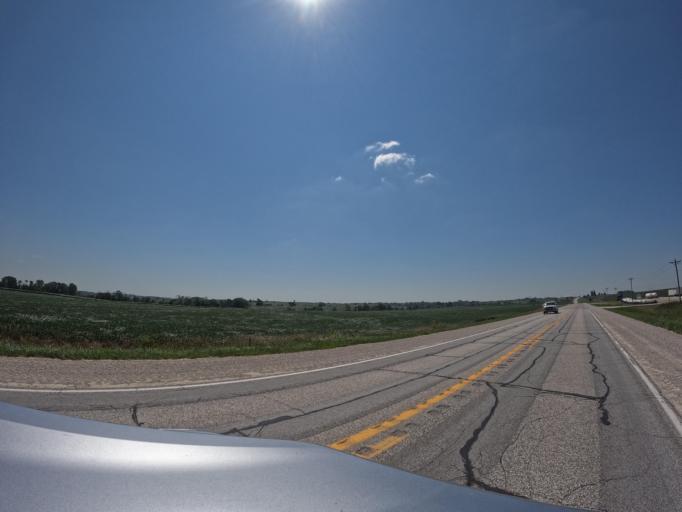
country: US
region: Iowa
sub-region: Keokuk County
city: Sigourney
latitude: 41.2890
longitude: -92.2046
